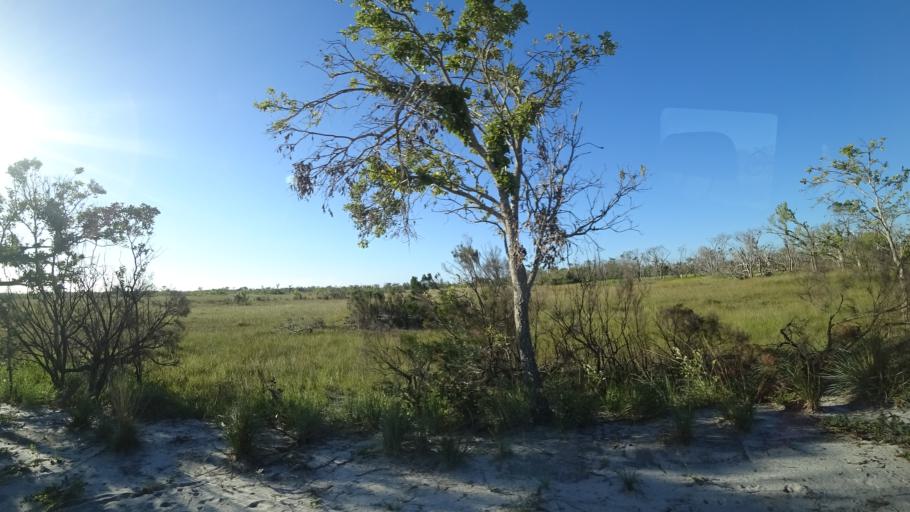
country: MZ
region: Sofala
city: Beira
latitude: -19.5793
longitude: 35.1767
